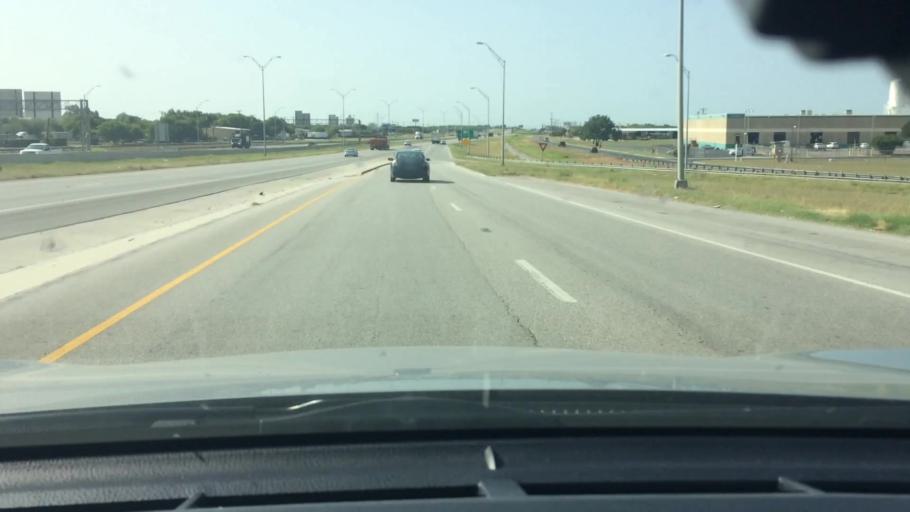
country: US
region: Texas
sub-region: Bexar County
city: Kirby
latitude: 29.4341
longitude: -98.3898
